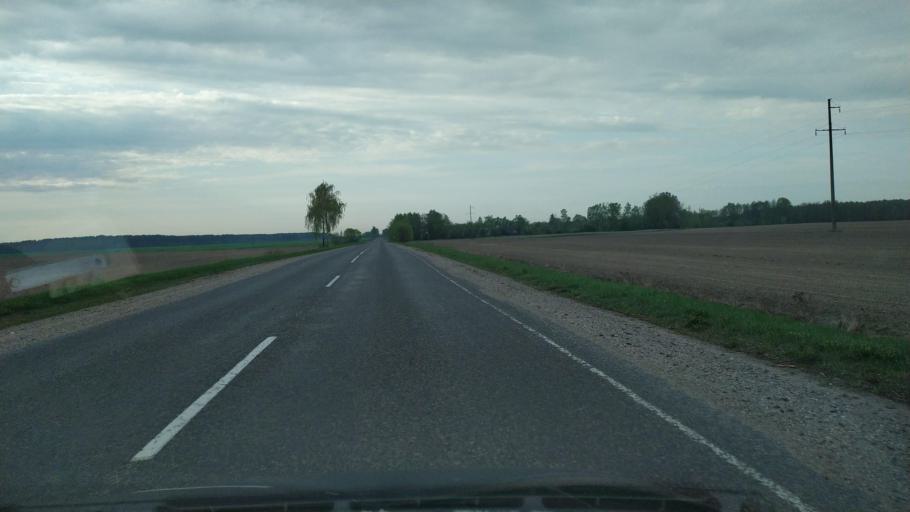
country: BY
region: Brest
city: Zhabinka
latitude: 52.2602
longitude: 23.9631
